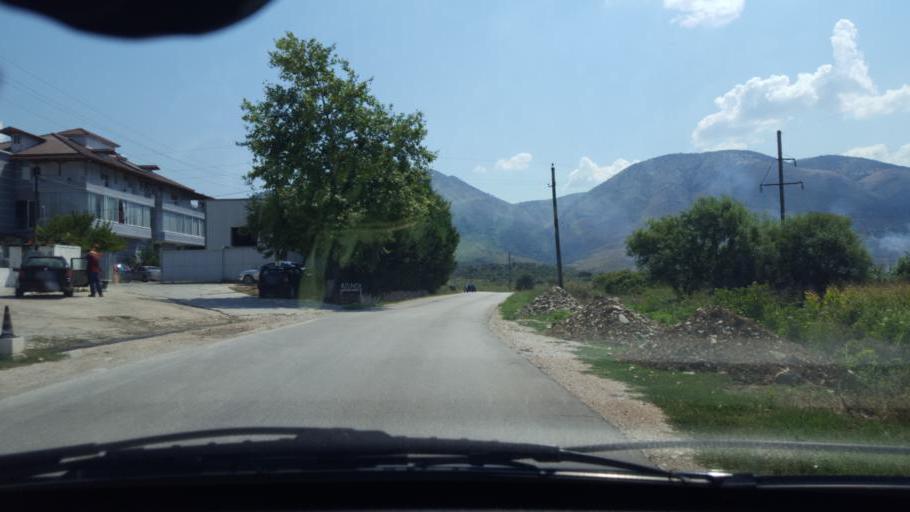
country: AL
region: Vlore
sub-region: Rrethi i Delvines
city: Mesopotam
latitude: 39.9117
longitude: 20.1069
